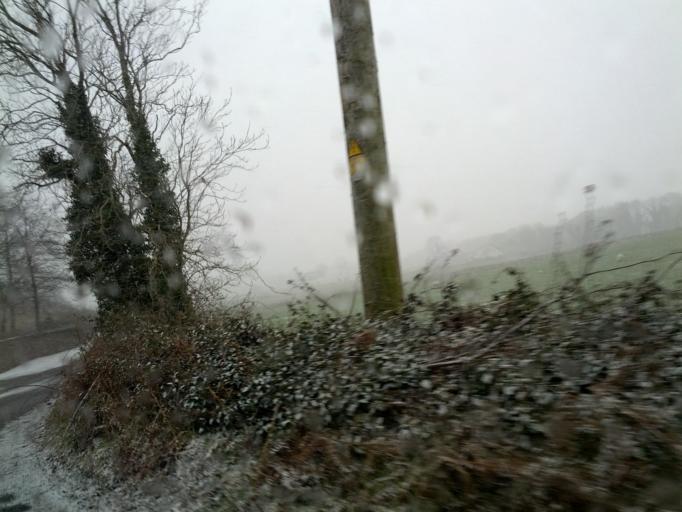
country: IE
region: Connaught
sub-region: County Galway
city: Oranmore
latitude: 53.2058
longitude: -8.8891
